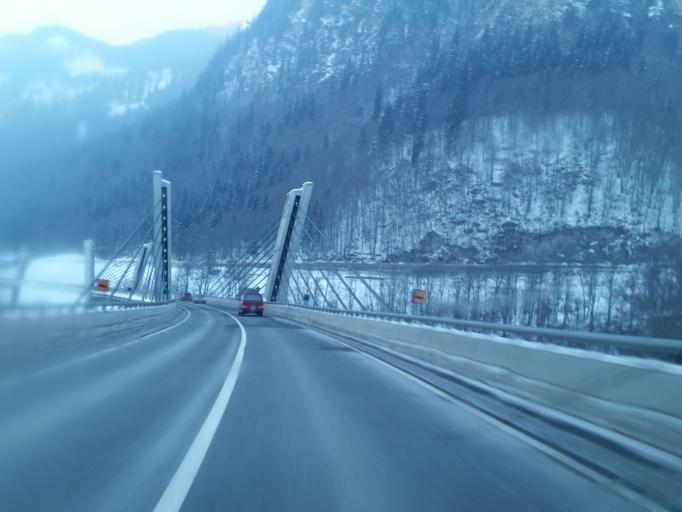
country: CH
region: Grisons
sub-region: Praettigau/Davos District
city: Klosters Serneus
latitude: 46.8837
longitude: 9.8575
